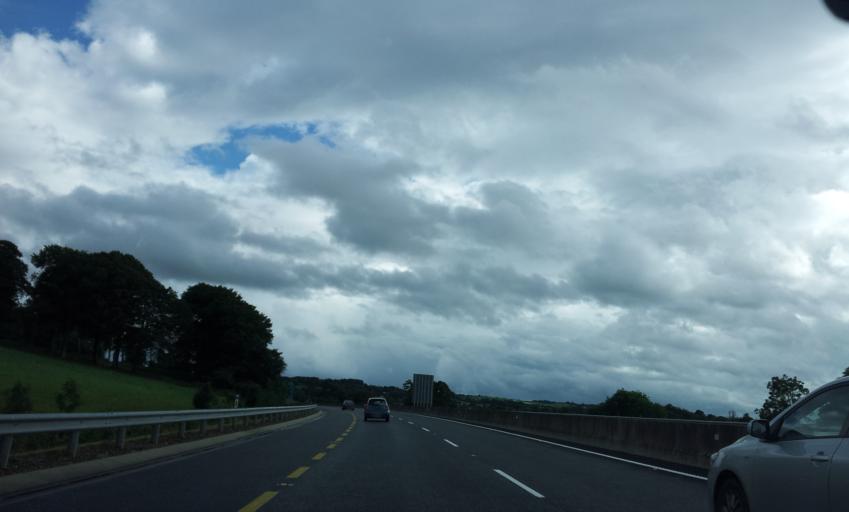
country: IE
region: Leinster
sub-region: Kilkenny
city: Mooncoin
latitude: 52.2493
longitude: -7.1912
